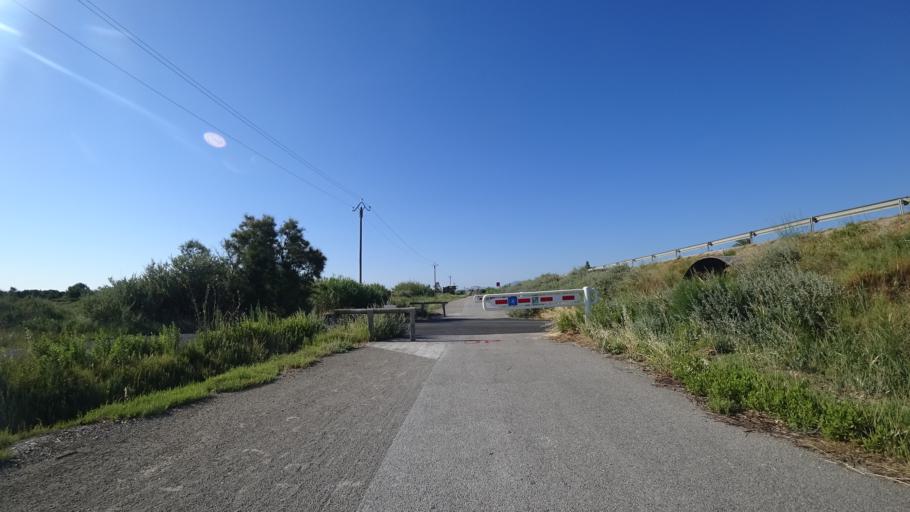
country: FR
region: Languedoc-Roussillon
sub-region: Departement des Pyrenees-Orientales
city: Sainte-Marie-Plage
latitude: 42.7429
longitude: 3.0238
